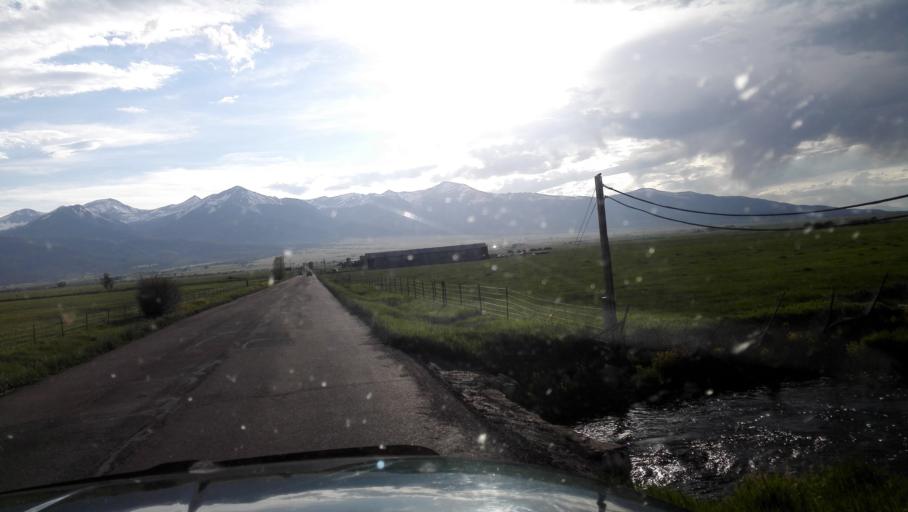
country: US
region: Colorado
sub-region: Custer County
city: Westcliffe
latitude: 38.1314
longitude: -105.4823
